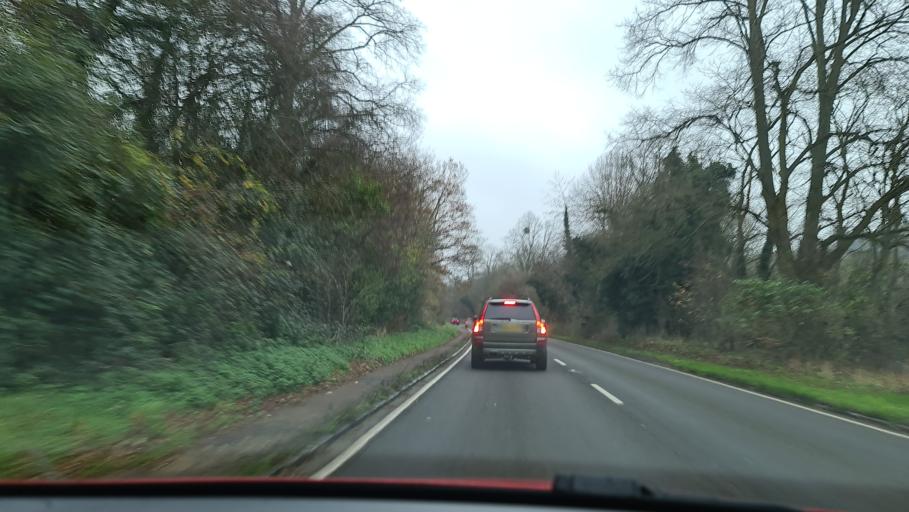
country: GB
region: England
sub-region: Buckinghamshire
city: Stokenchurch
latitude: 51.6403
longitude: -0.8269
